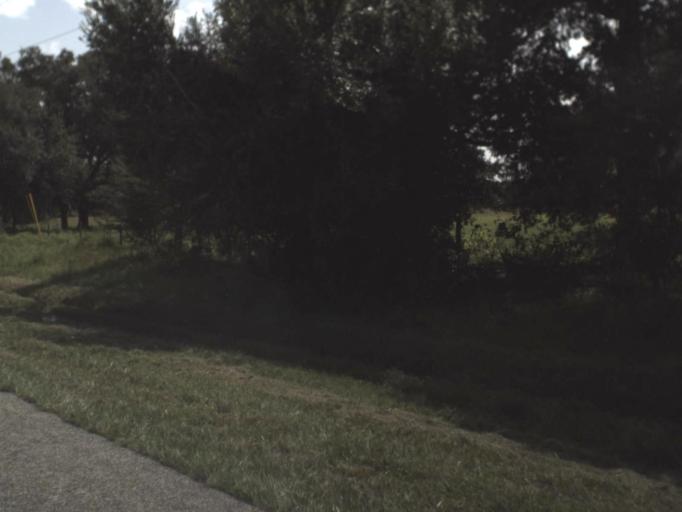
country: US
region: Florida
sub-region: Polk County
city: Lake Wales
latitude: 27.9402
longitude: -81.6132
